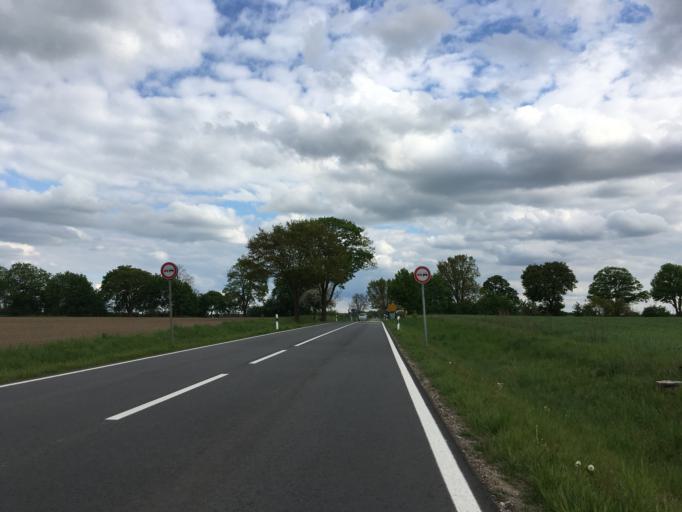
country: DE
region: Brandenburg
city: Bernau bei Berlin
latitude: 52.6557
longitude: 13.6012
